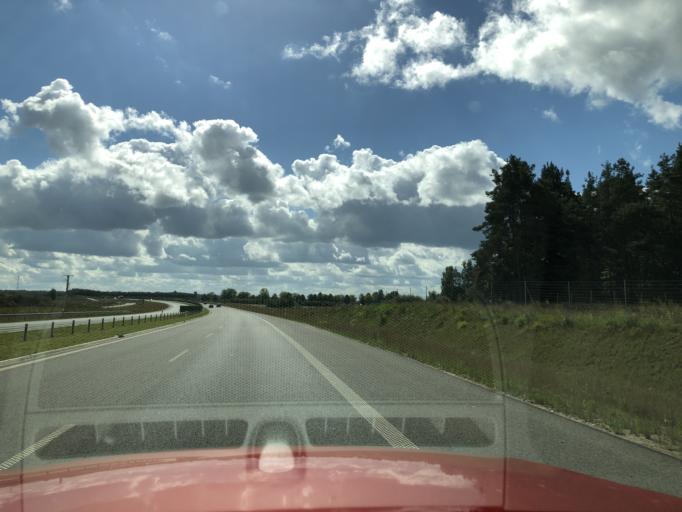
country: PL
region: West Pomeranian Voivodeship
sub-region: Powiat szczecinecki
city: Szczecinek
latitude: 53.6613
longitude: 16.7375
